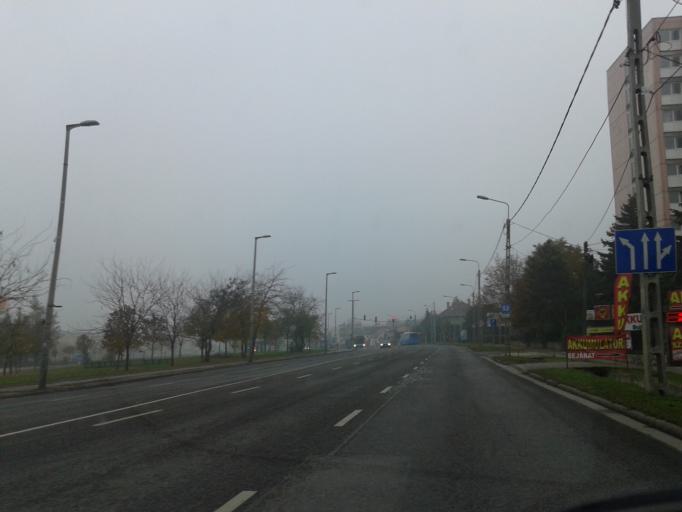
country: HU
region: Budapest
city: Budapest XXII. keruelet
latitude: 47.4093
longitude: 19.0183
